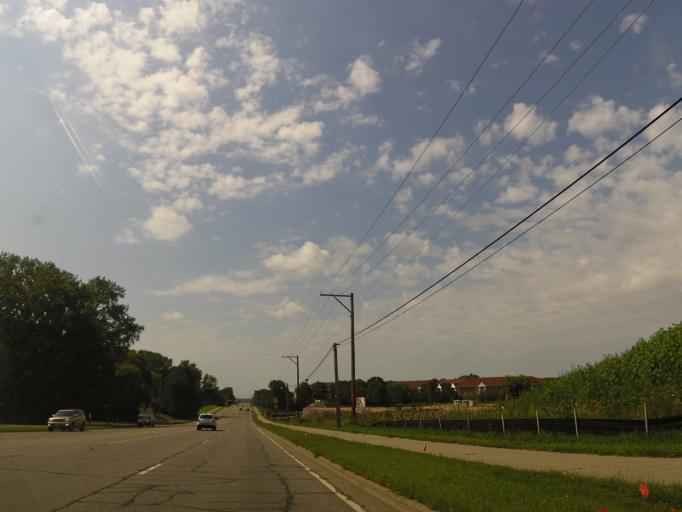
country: US
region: Minnesota
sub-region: Dakota County
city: Eagan
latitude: 44.8336
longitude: -93.1742
